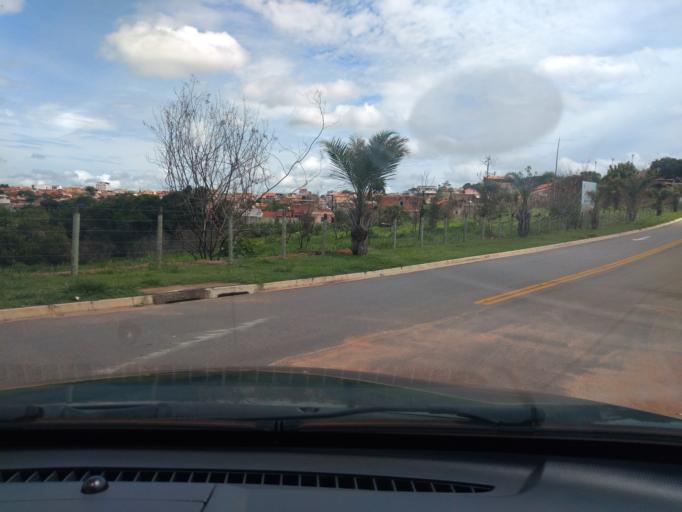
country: BR
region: Minas Gerais
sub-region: Tres Coracoes
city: Tres Coracoes
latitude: -21.6786
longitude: -45.2743
